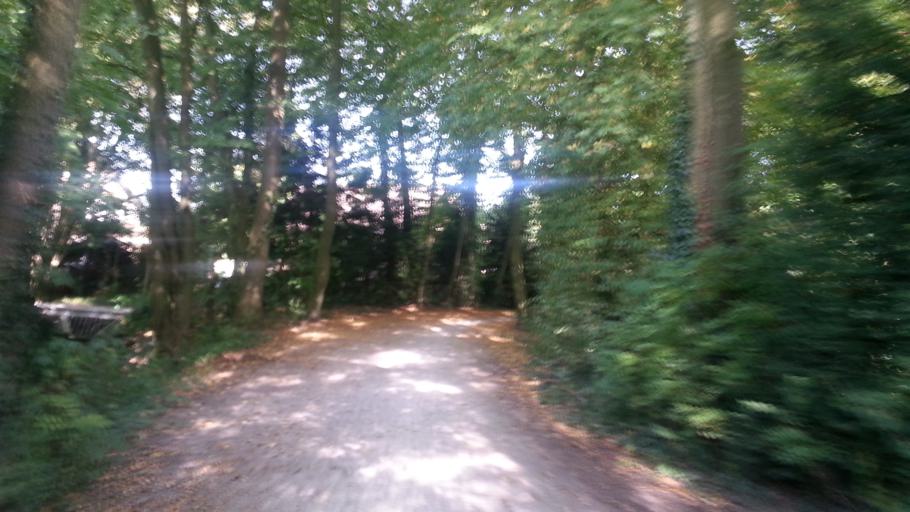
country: DE
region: North Rhine-Westphalia
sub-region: Regierungsbezirk Munster
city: Muenster
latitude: 51.9982
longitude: 7.5883
